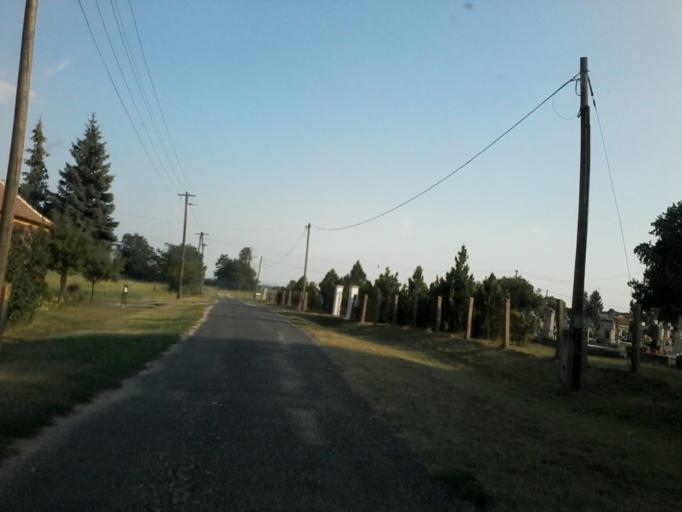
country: HU
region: Vas
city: Janoshaza
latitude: 47.1140
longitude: 17.2011
